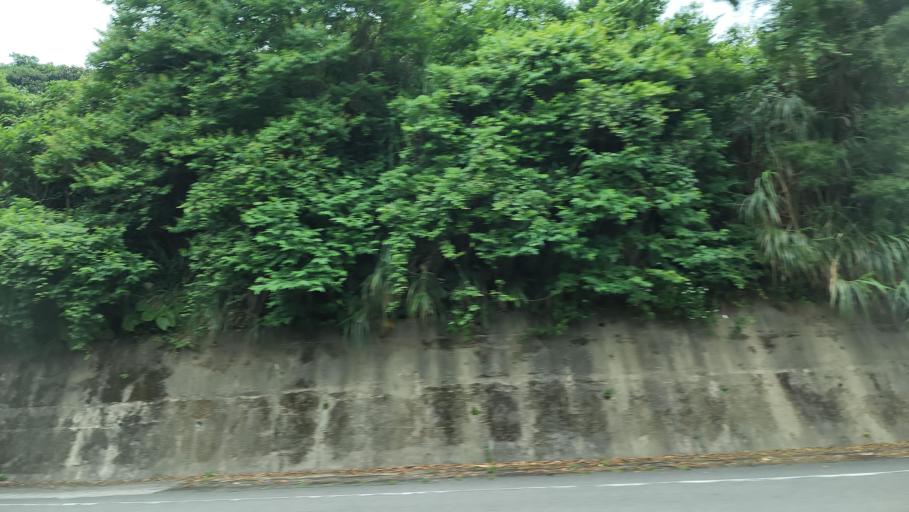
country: TW
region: Taiwan
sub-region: Keelung
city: Keelung
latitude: 25.1964
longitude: 121.6829
